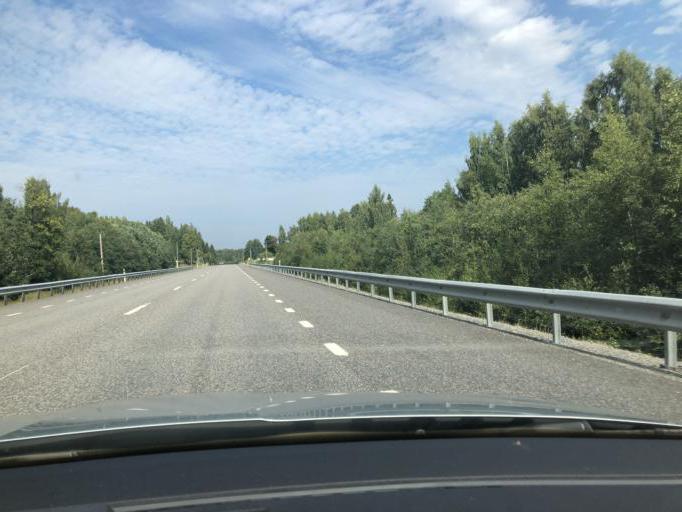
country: SE
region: Vaesternorrland
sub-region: Kramfors Kommun
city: Kramfors
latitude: 62.8457
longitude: 17.8749
